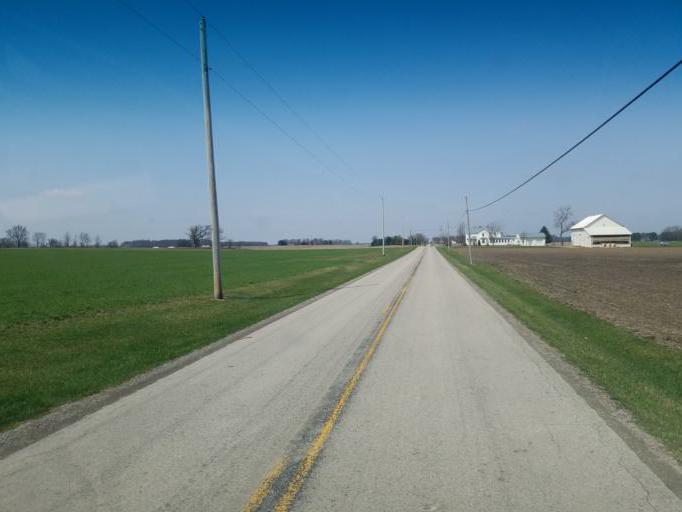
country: US
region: Ohio
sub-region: Wyandot County
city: Upper Sandusky
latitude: 40.8764
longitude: -83.2612
